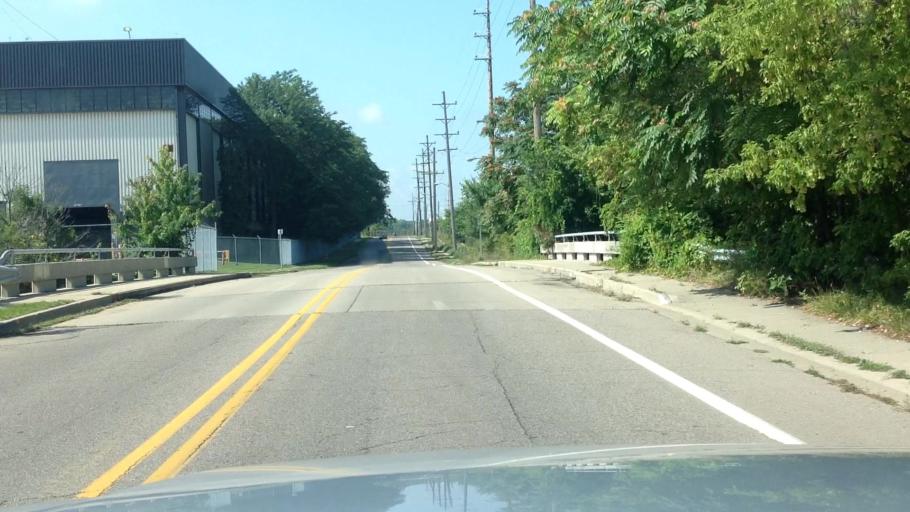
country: US
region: Michigan
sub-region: Genesee County
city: Flint
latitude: 43.0138
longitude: -83.6983
